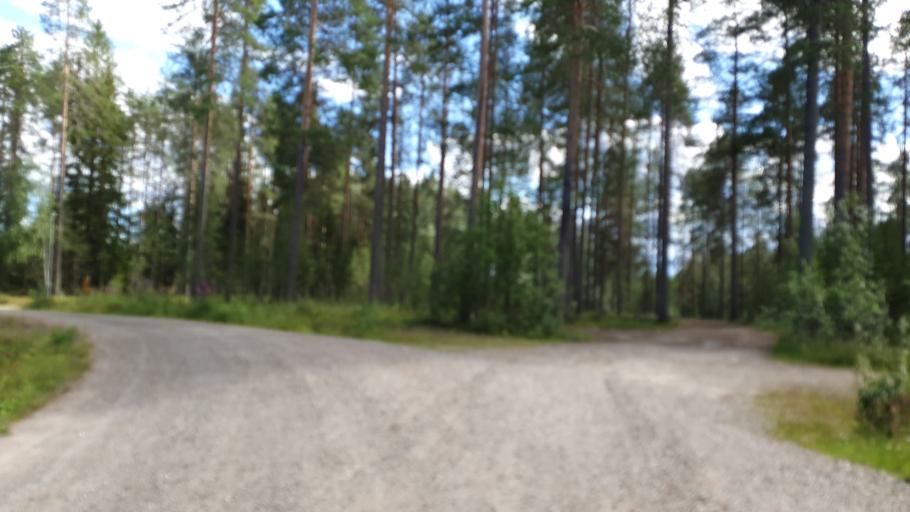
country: FI
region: Kainuu
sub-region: Kehys-Kainuu
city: Kuhmo
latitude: 64.1150
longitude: 29.5165
